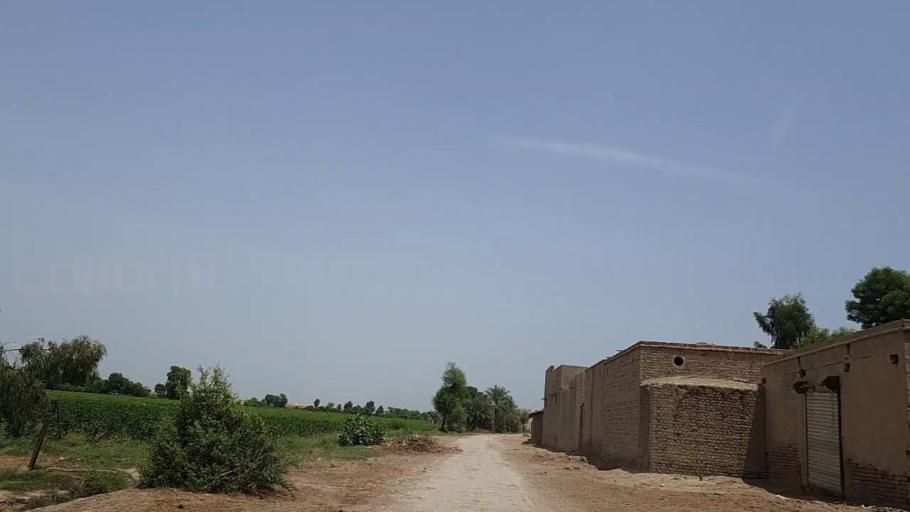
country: PK
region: Sindh
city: Tharu Shah
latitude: 26.9664
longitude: 68.0344
